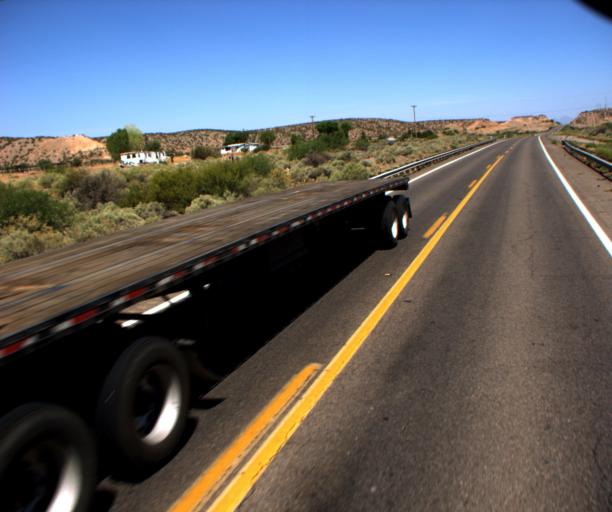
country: US
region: Arizona
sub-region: Graham County
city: Bylas
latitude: 33.0979
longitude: -110.0768
